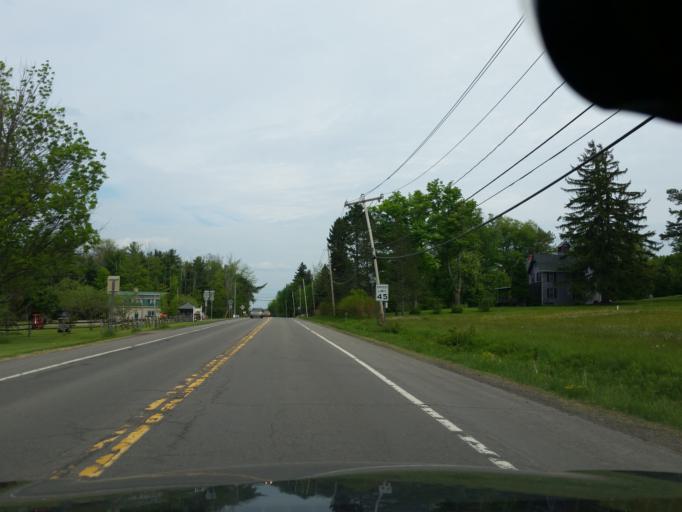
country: US
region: New York
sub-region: Chautauqua County
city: Lakewood
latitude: 42.1109
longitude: -79.3849
